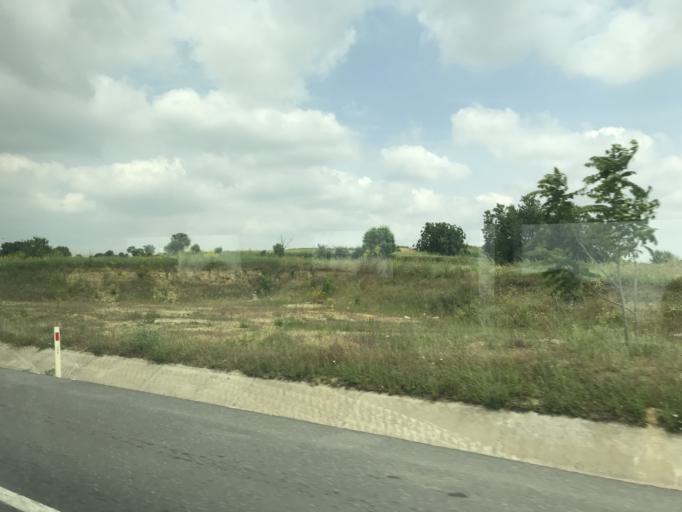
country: TR
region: Tekirdag
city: Tekirdag
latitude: 40.9935
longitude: 27.5611
